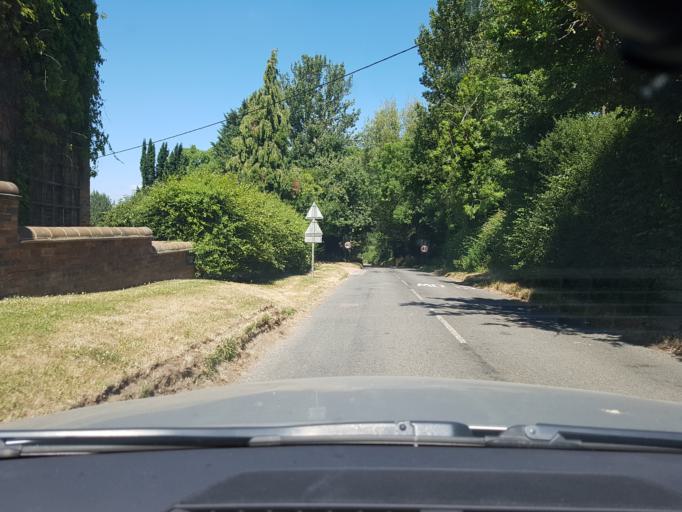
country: GB
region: England
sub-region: Milton Keynes
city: Calverton
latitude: 52.0324
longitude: -0.8365
